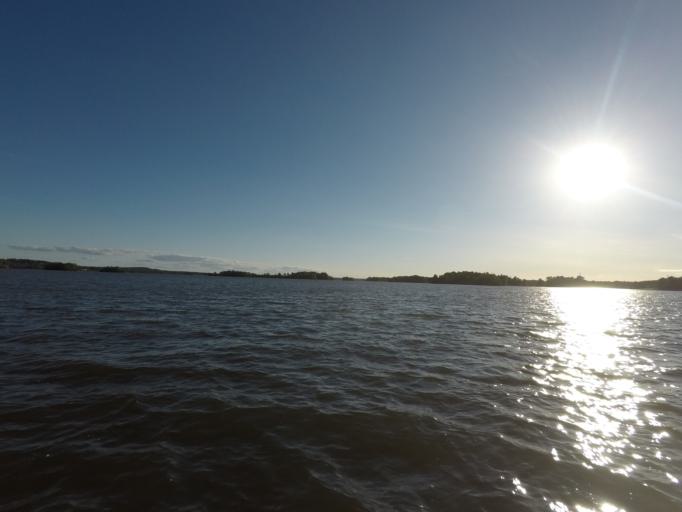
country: SE
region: Soedermanland
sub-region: Eskilstuna Kommun
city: Torshalla
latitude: 59.4799
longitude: 16.4694
